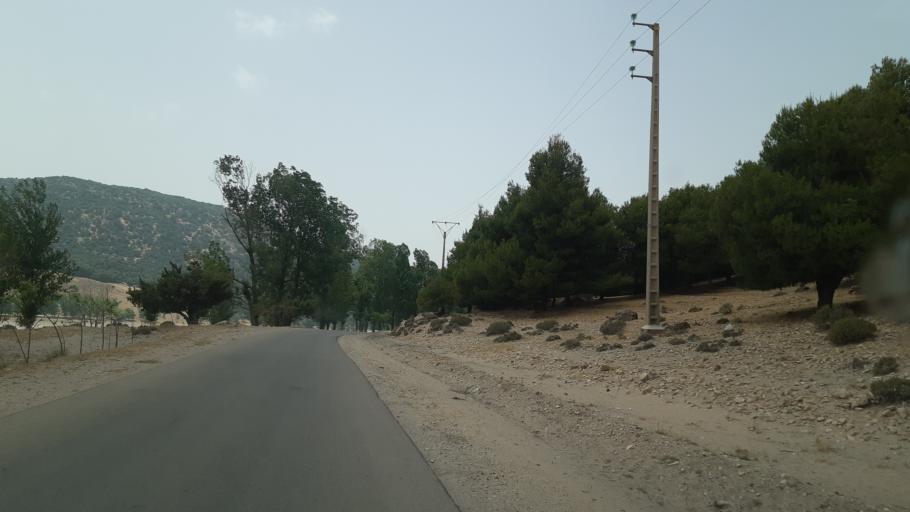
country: MA
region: Meknes-Tafilalet
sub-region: Ifrane
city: Ifrane
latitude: 33.6541
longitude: -5.0311
